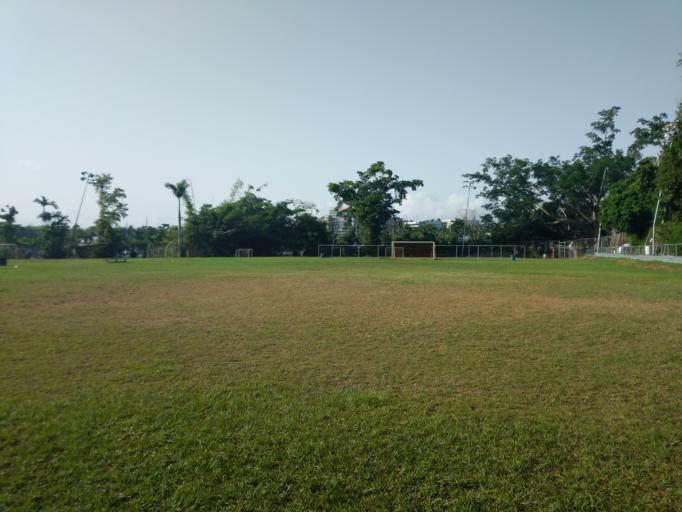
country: PR
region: Guaynabo
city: Guaynabo
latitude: 18.3807
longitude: -66.0750
